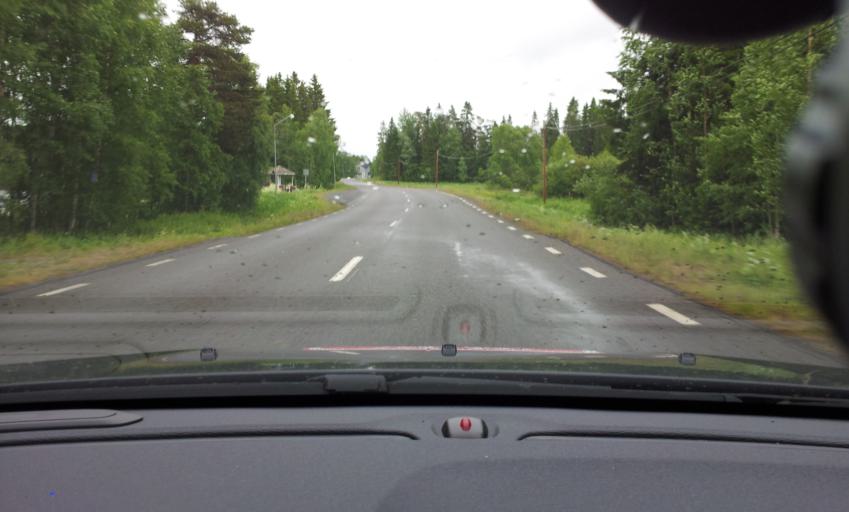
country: SE
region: Jaemtland
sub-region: OEstersunds Kommun
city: Lit
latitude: 63.6713
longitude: 15.0838
